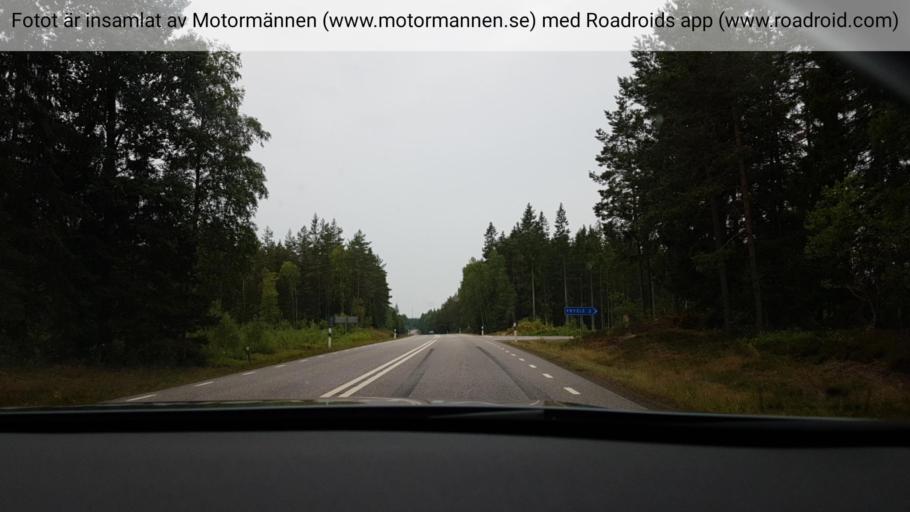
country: SE
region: Joenkoeping
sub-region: Varnamo Kommun
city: Bor
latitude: 57.2555
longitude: 14.1830
